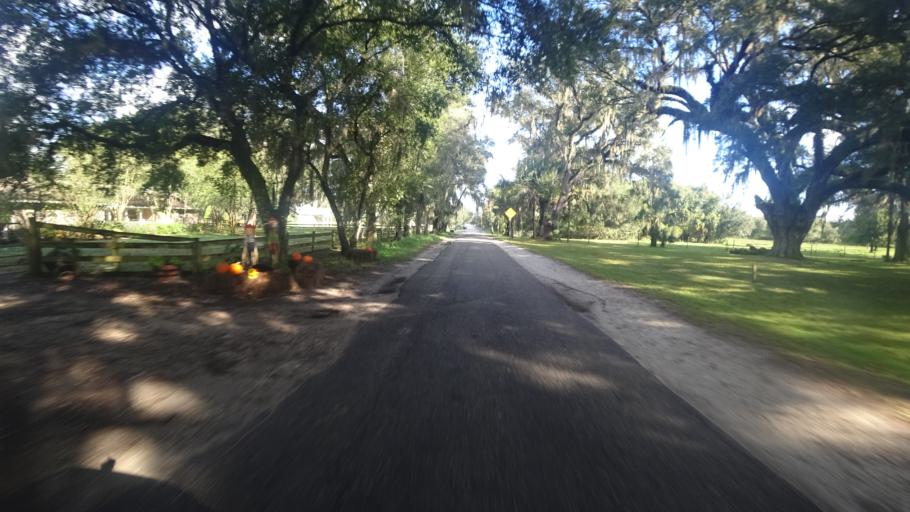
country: US
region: Florida
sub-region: Manatee County
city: Ellenton
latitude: 27.5696
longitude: -82.3924
